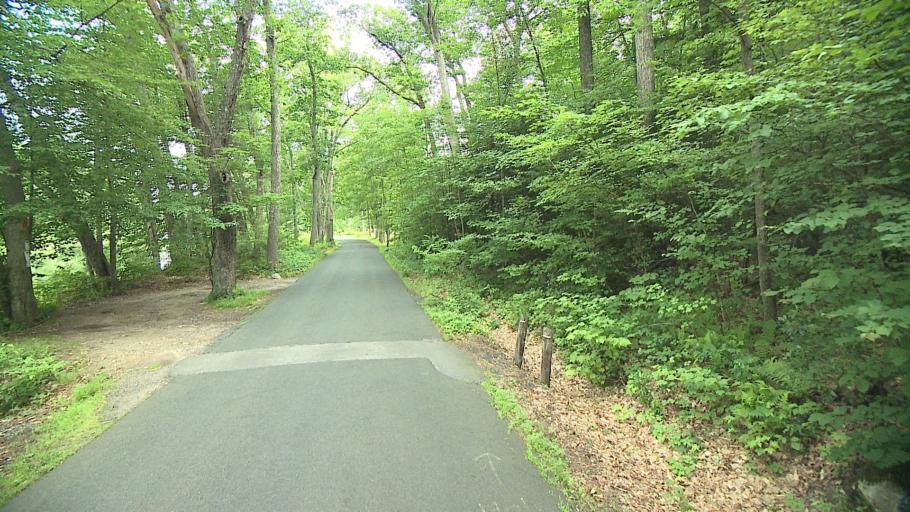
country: US
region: Connecticut
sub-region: Litchfield County
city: Winsted
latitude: 41.9536
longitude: -73.0125
